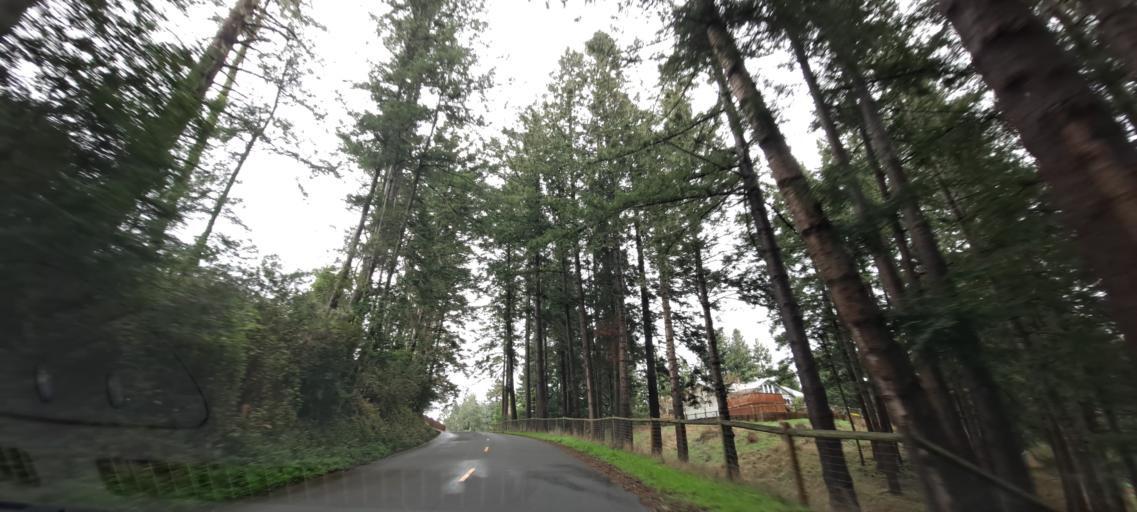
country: US
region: California
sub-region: Humboldt County
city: Fortuna
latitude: 40.5998
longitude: -124.1401
